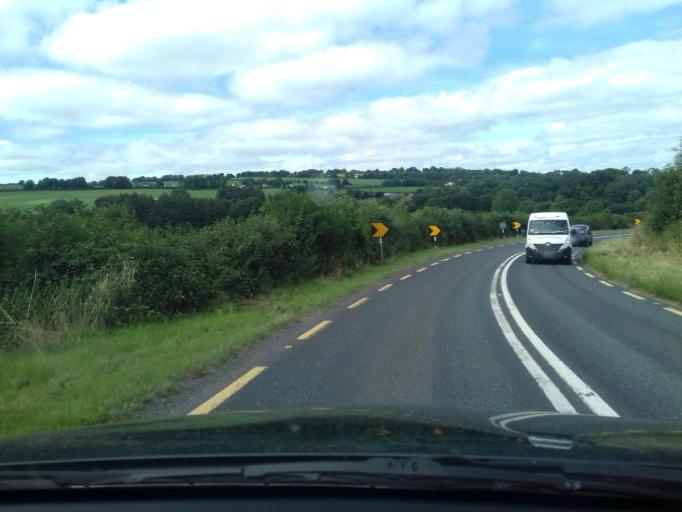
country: IE
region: Leinster
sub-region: Wicklow
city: Baltinglass
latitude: 52.9775
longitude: -6.6843
